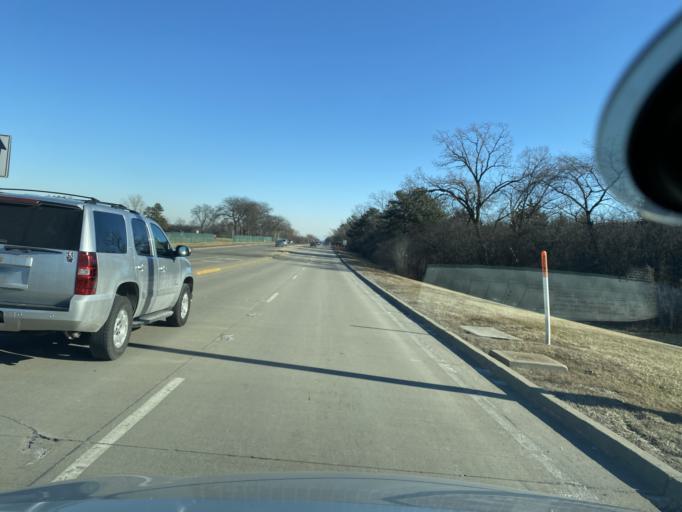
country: US
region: Illinois
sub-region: DuPage County
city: Oak Brook
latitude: 41.8478
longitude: -87.9169
